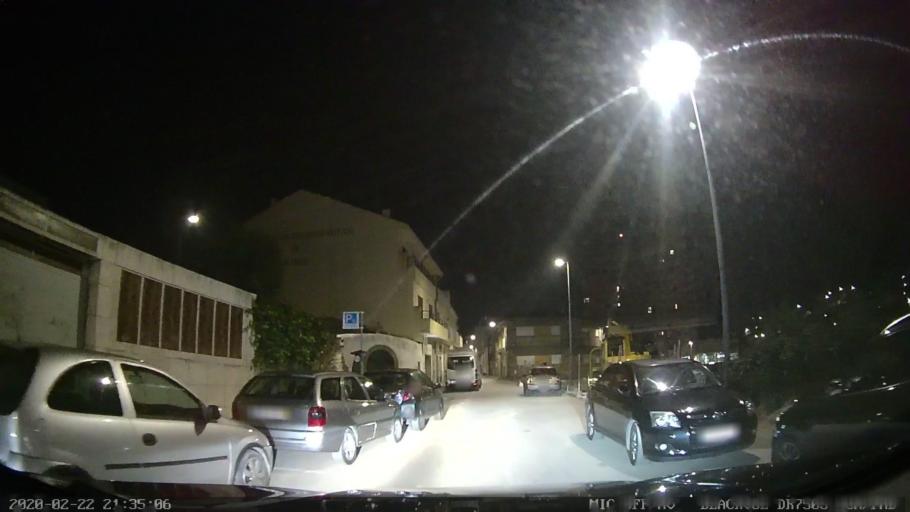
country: PT
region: Porto
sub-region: Valongo
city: Valongo
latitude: 41.1883
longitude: -8.4957
